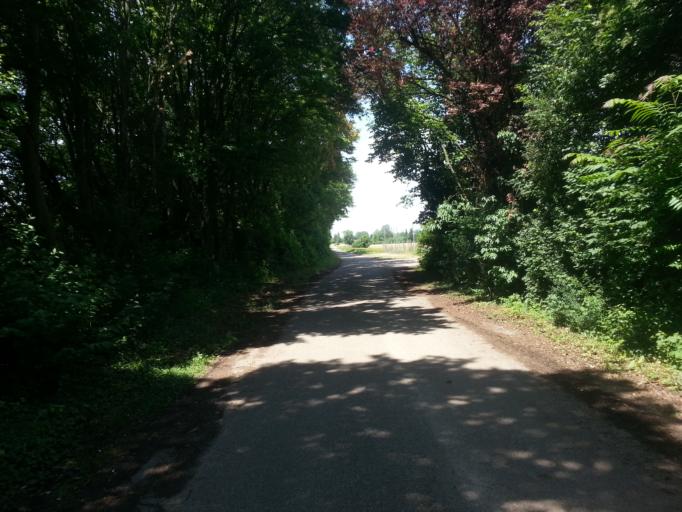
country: DE
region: Baden-Wuerttemberg
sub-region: Karlsruhe Region
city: Eppelheim
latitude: 49.4352
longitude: 8.6324
